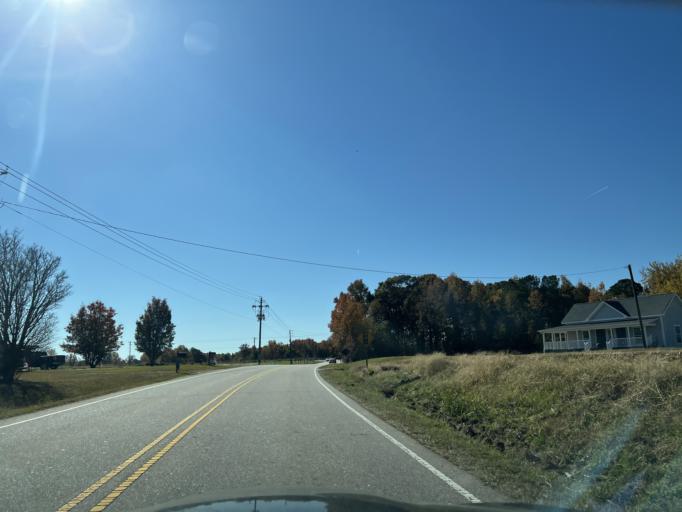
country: US
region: North Carolina
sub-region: Wake County
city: Garner
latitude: 35.6728
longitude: -78.7051
